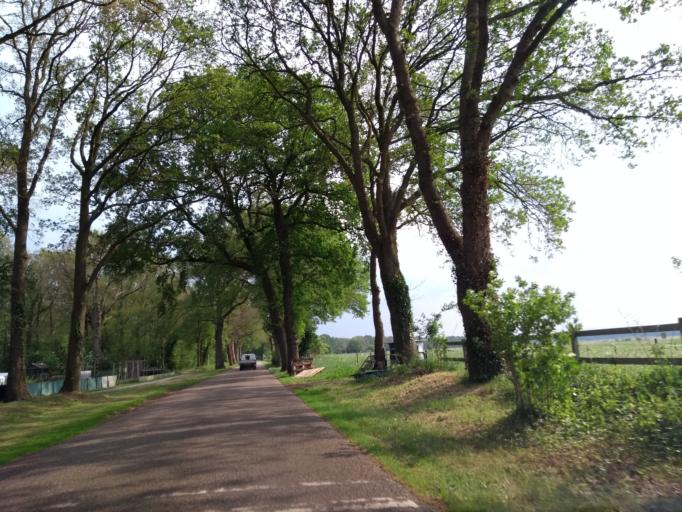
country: NL
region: Overijssel
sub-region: Gemeente Staphorst
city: Staphorst
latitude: 52.6544
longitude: 6.2914
